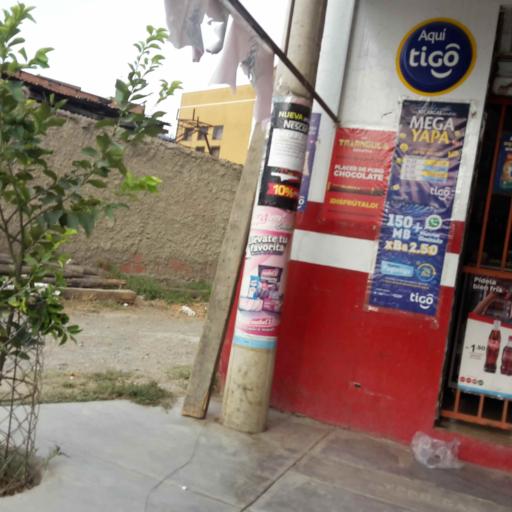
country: BO
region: Cochabamba
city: Cochabamba
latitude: -17.3645
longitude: -66.1893
